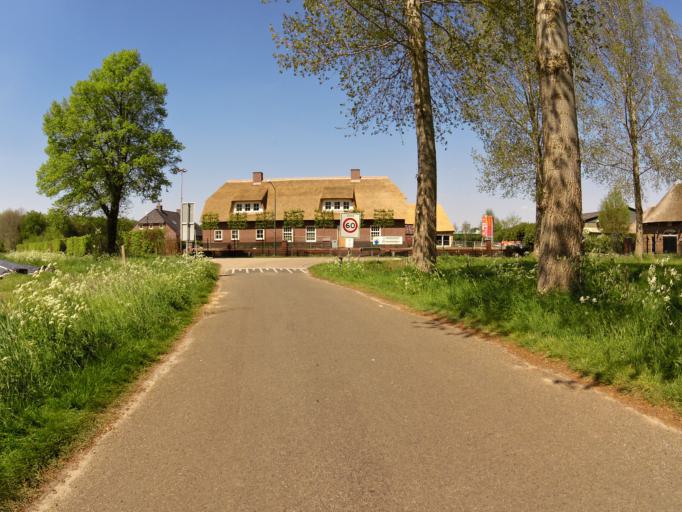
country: NL
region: North Brabant
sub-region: Gemeente Haaren
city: Haaren
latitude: 51.6597
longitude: 5.2131
